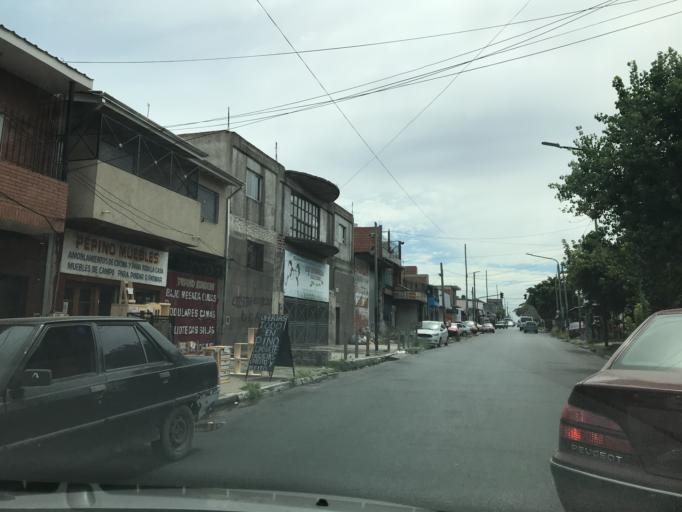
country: AR
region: Buenos Aires
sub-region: Partido de Lomas de Zamora
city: Lomas de Zamora
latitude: -34.7324
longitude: -58.4281
